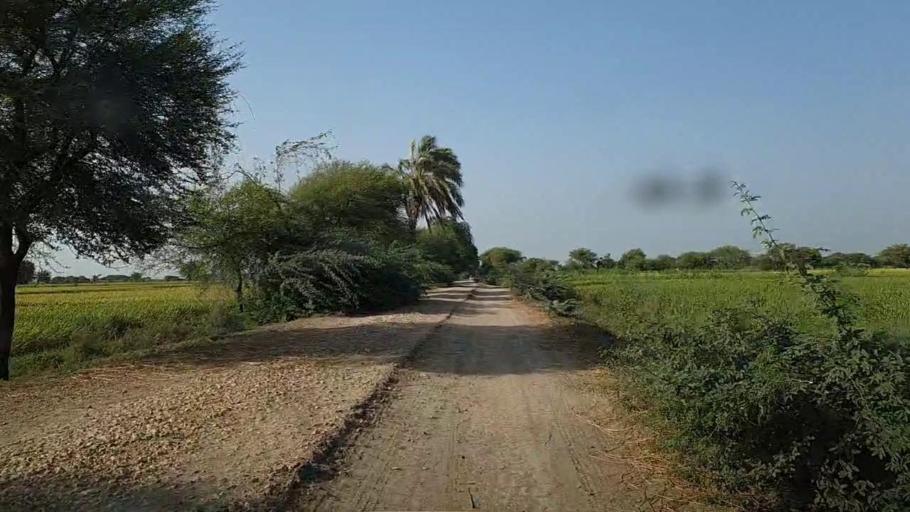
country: PK
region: Sindh
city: Bulri
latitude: 24.7784
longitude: 68.4336
